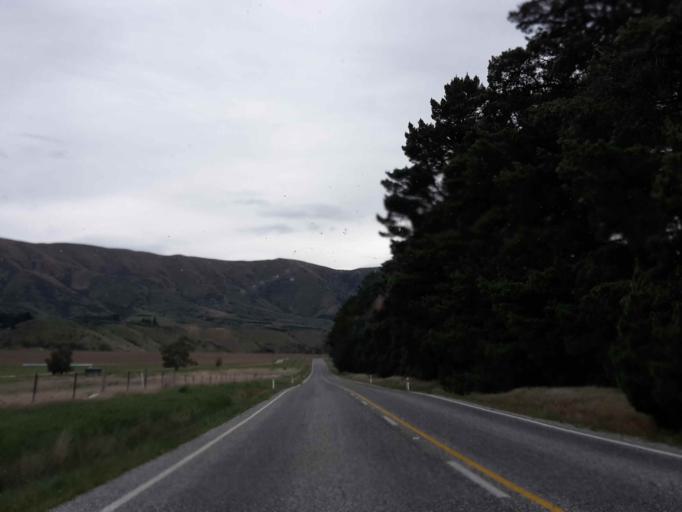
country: NZ
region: Otago
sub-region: Queenstown-Lakes District
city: Wanaka
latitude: -44.7333
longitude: 169.3046
